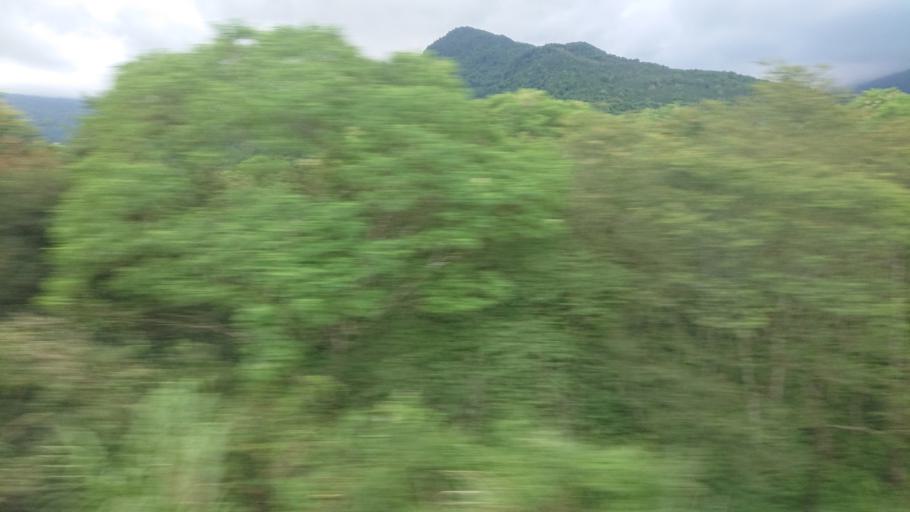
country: TW
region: Taiwan
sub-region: Hualien
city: Hualian
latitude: 23.6172
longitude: 121.3941
